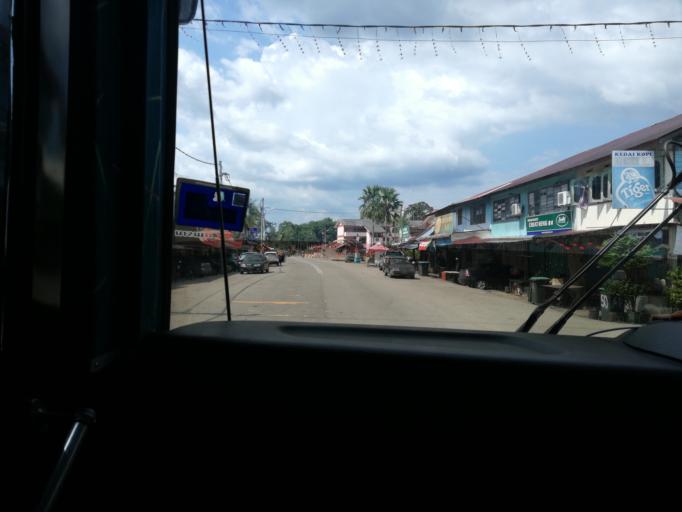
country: MY
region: Perak
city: Parit Buntar
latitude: 5.1407
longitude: 100.5904
